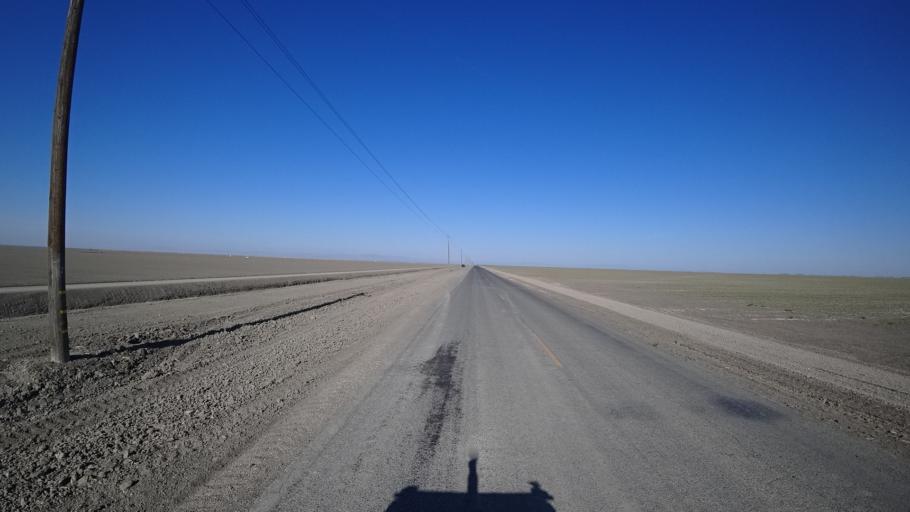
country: US
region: California
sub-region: Kings County
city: Stratford
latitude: 36.0797
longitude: -119.7198
